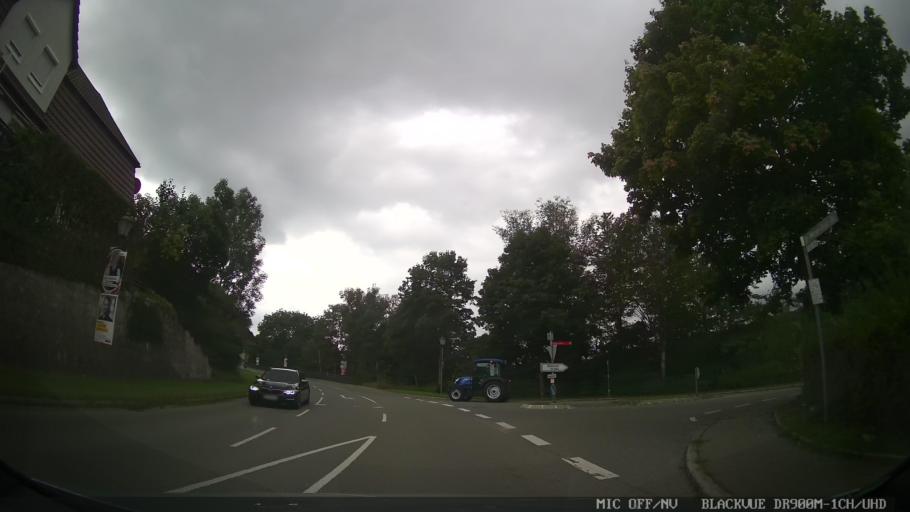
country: DE
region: Baden-Wuerttemberg
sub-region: Freiburg Region
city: Fridingen an der Donau
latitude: 48.0289
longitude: 8.9361
